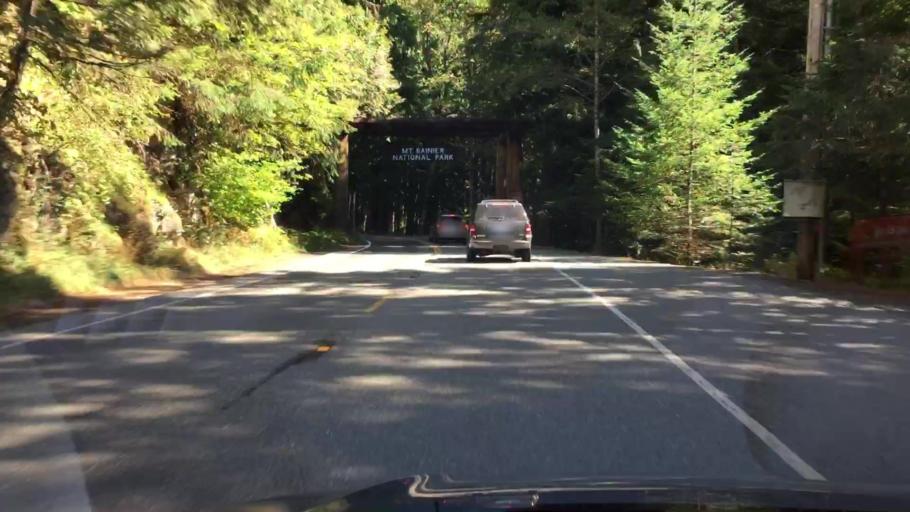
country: US
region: Washington
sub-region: Pierce County
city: Eatonville
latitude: 46.7414
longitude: -121.9190
